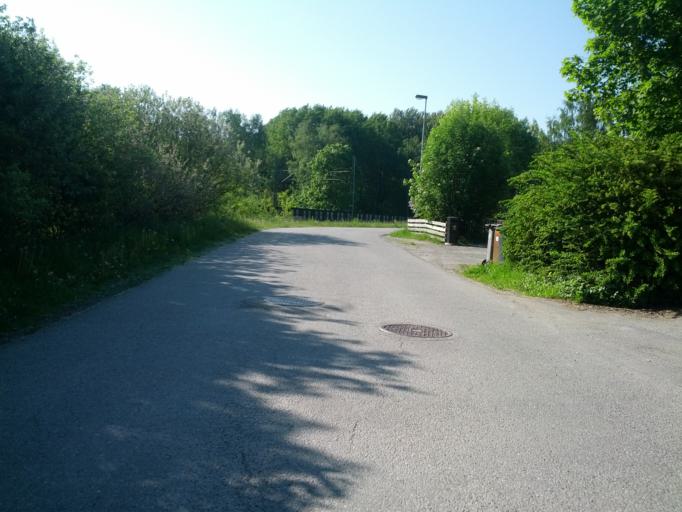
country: SE
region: Stockholm
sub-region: Danderyds Kommun
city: Djursholm
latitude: 59.4248
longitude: 18.0506
